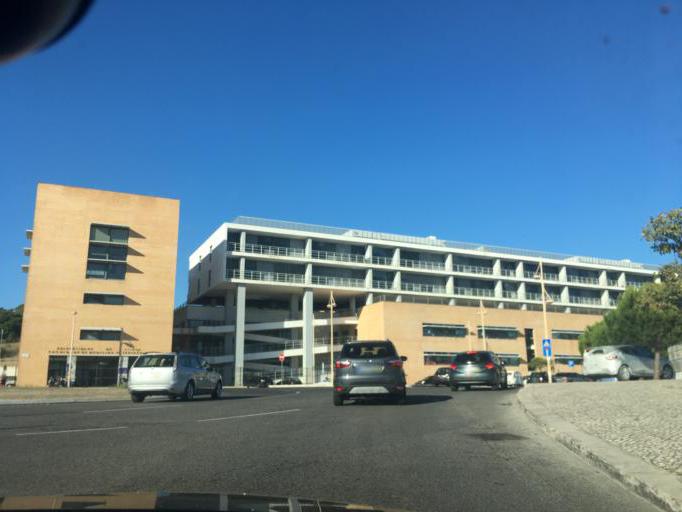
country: PT
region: Lisbon
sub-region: Oeiras
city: Alges
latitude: 38.7134
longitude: -9.1955
